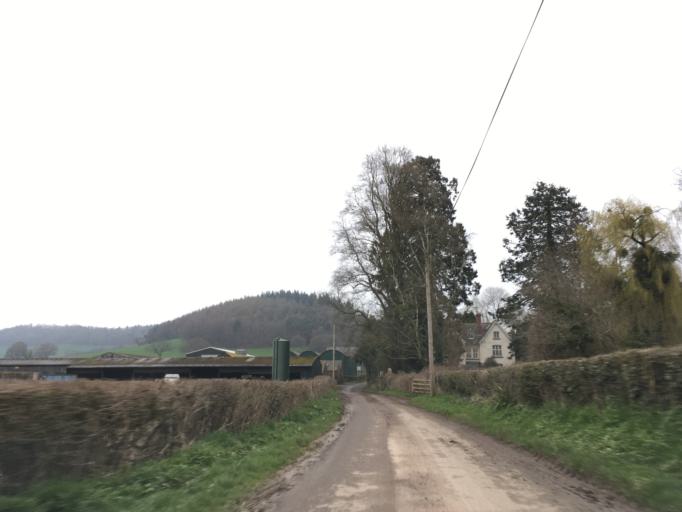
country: GB
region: Wales
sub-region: Monmouthshire
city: Usk
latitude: 51.7234
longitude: -2.9129
